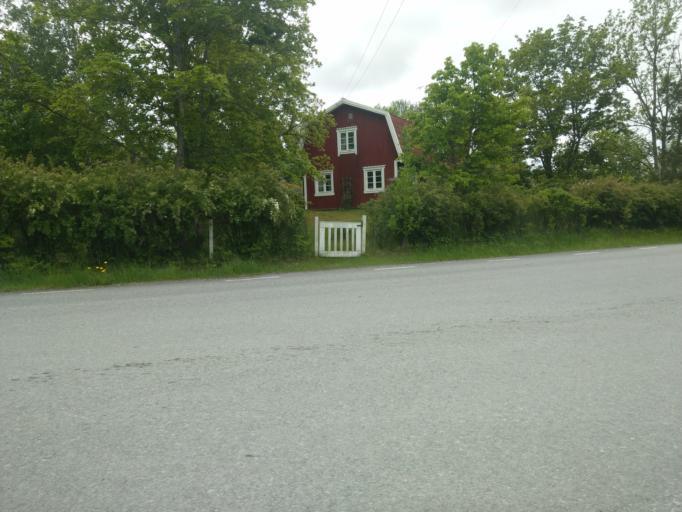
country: SE
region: Stockholm
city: Stenhamra
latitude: 59.4060
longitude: 17.6294
